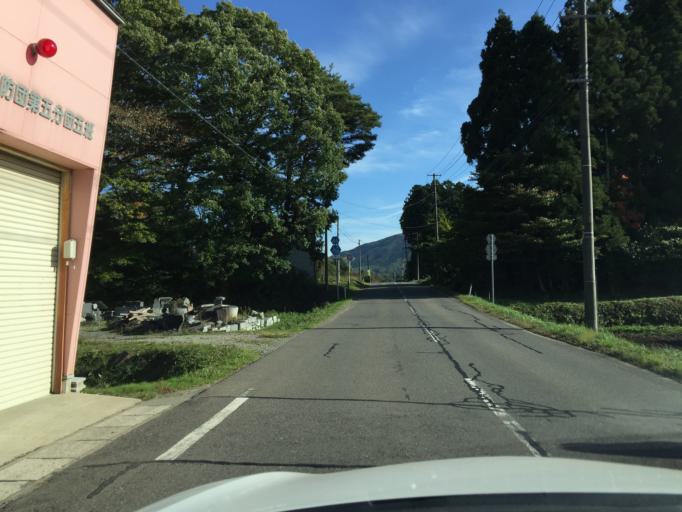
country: JP
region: Fukushima
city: Funehikimachi-funehiki
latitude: 37.3524
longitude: 140.5509
